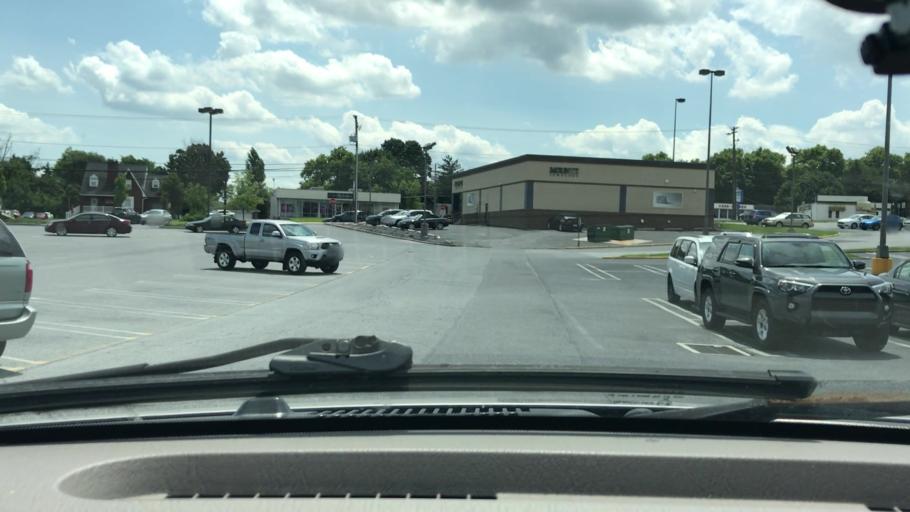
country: US
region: Pennsylvania
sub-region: Dauphin County
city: Colonial Park
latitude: 40.3016
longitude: -76.8173
